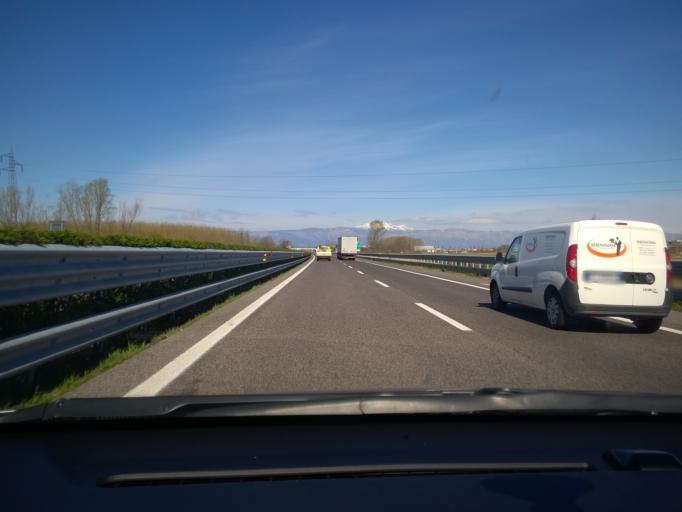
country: IT
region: Veneto
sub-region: Provincia di Venezia
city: Cinto Caomaggiore
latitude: 45.8545
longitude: 12.7803
